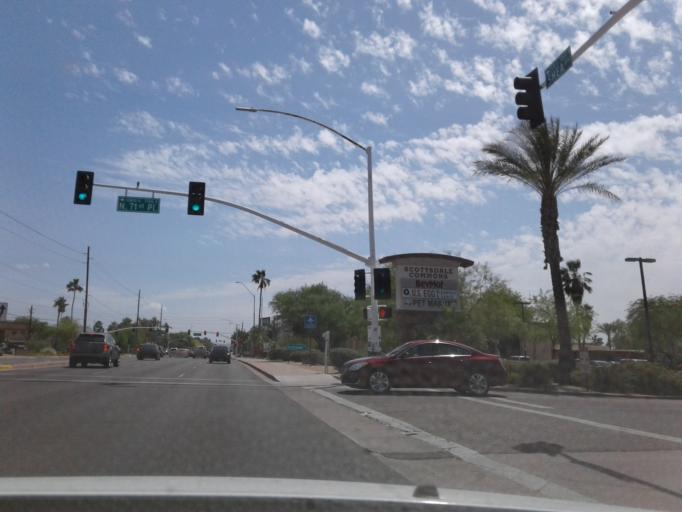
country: US
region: Arizona
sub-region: Maricopa County
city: Paradise Valley
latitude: 33.5812
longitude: -111.9279
